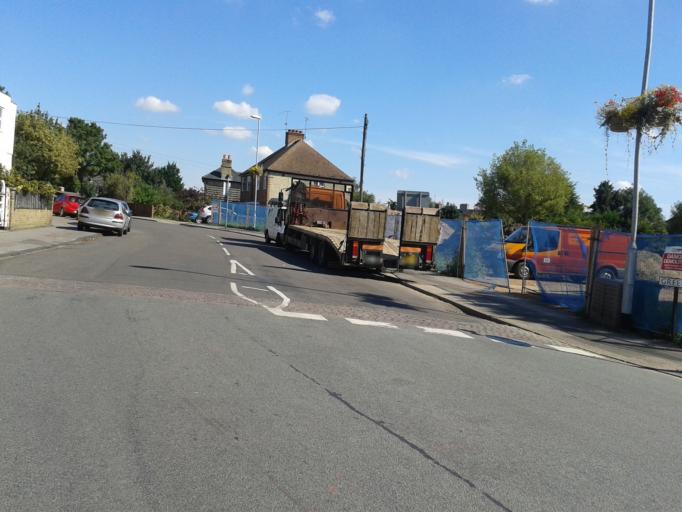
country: GB
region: England
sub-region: Cambridgeshire
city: Cambridge
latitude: 52.2192
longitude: 0.1464
